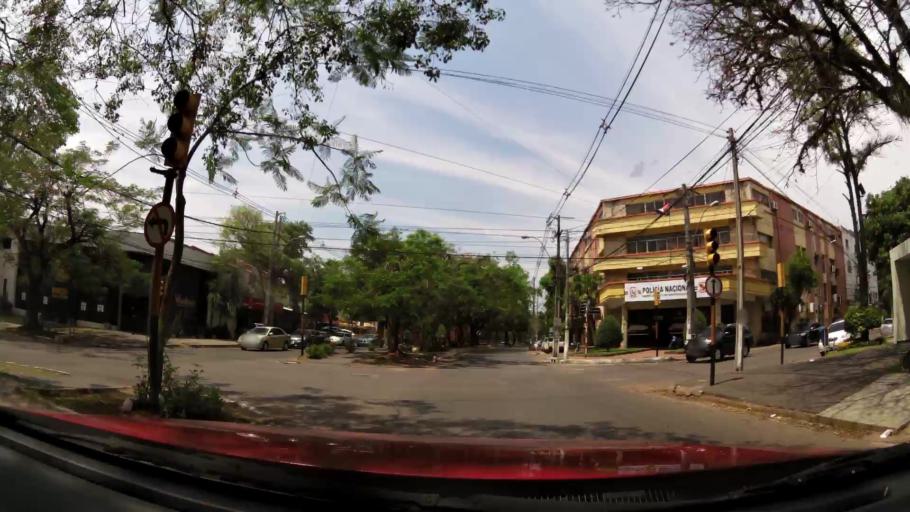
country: PY
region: Central
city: Fernando de la Mora
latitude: -25.3014
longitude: -57.5659
